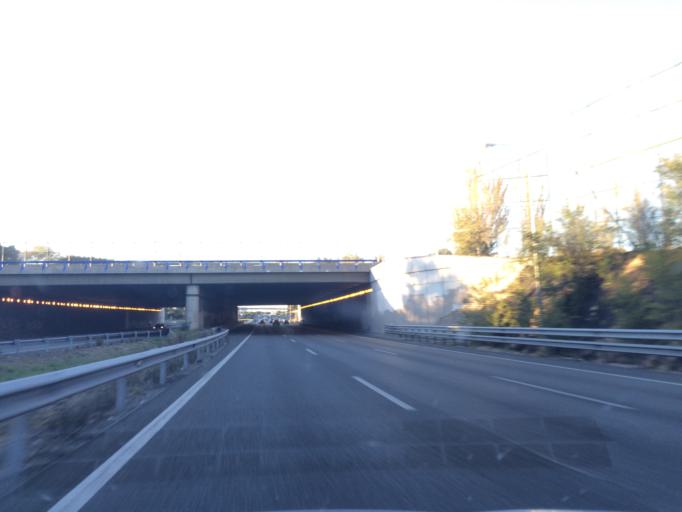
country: ES
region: Madrid
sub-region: Provincia de Madrid
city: Alcorcon
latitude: 40.3702
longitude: -3.7993
